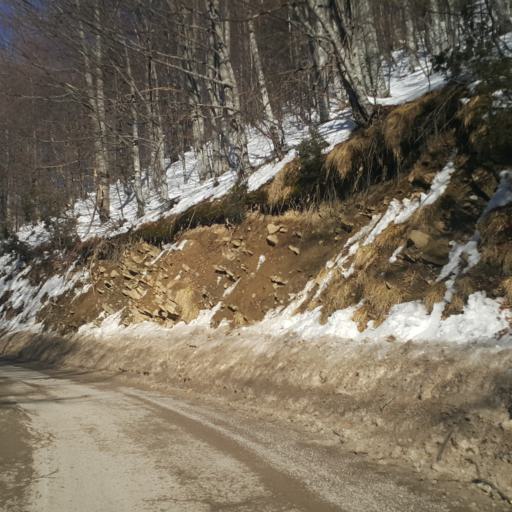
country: XK
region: Mitrovica
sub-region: Komuna e Leposaviqit
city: Leposaviq
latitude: 43.3117
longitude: 20.8617
